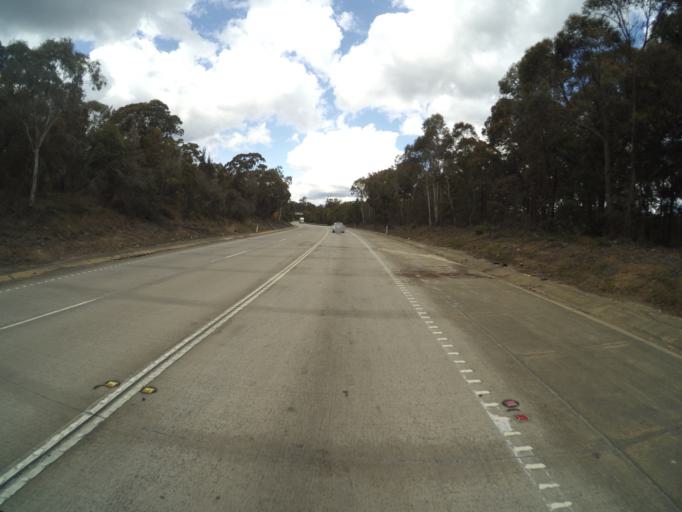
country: AU
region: New South Wales
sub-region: Wollondilly
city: Douglas Park
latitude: -34.2703
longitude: 150.7136
